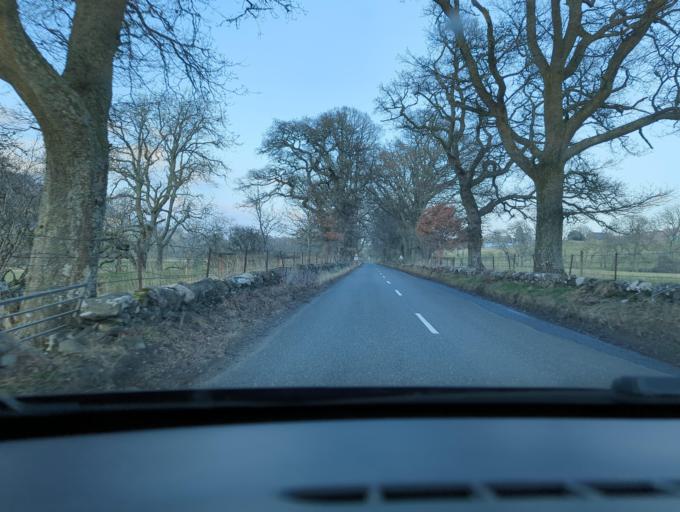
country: GB
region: Scotland
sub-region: Perth and Kinross
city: Methven
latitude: 56.5425
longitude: -3.6563
